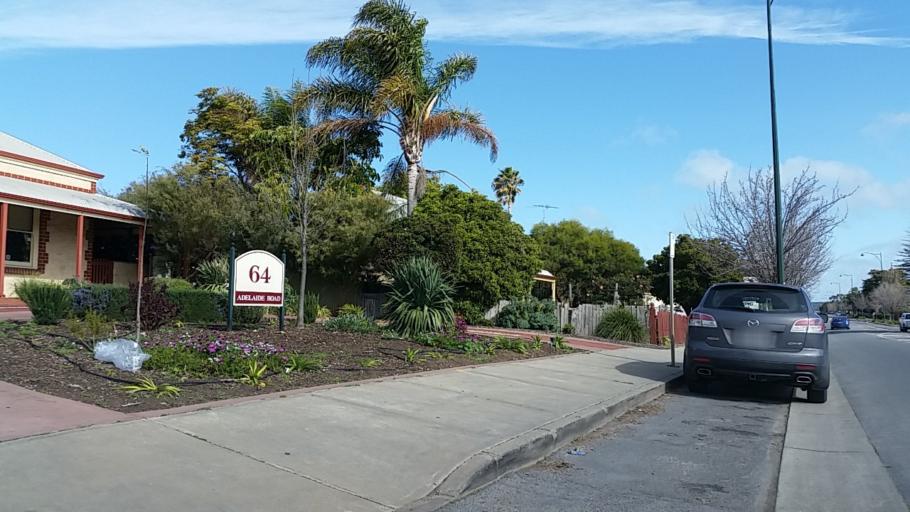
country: AU
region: South Australia
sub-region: Murray Bridge
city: Murray Bridge
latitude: -35.1221
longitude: 139.2688
